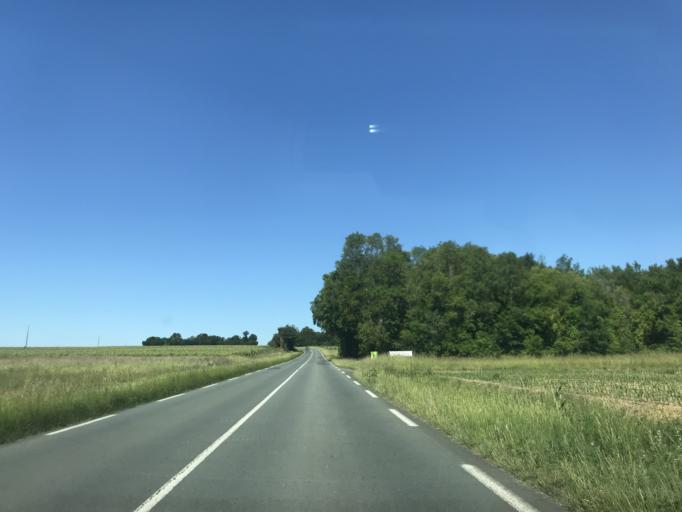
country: FR
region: Poitou-Charentes
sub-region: Departement de la Charente-Maritime
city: Gemozac
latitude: 45.5713
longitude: -0.6256
